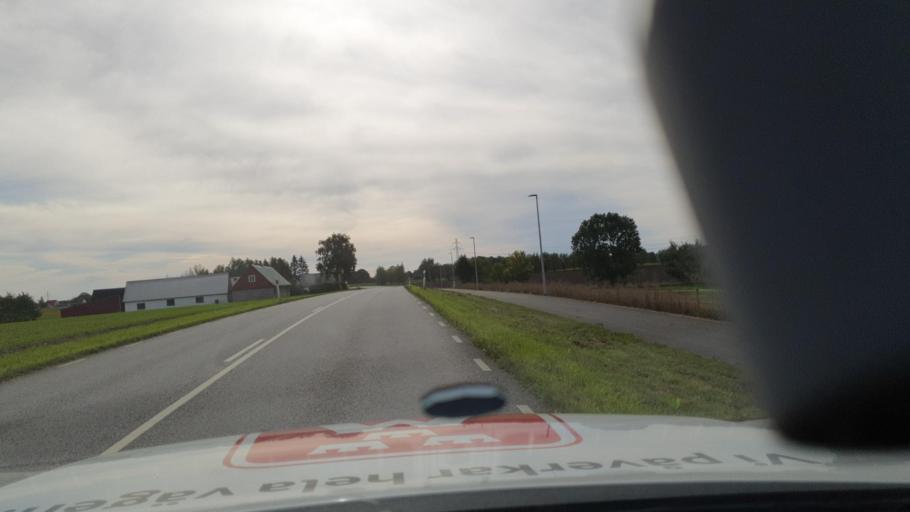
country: SE
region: Skane
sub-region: Malmo
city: Oxie
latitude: 55.5233
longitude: 13.0827
